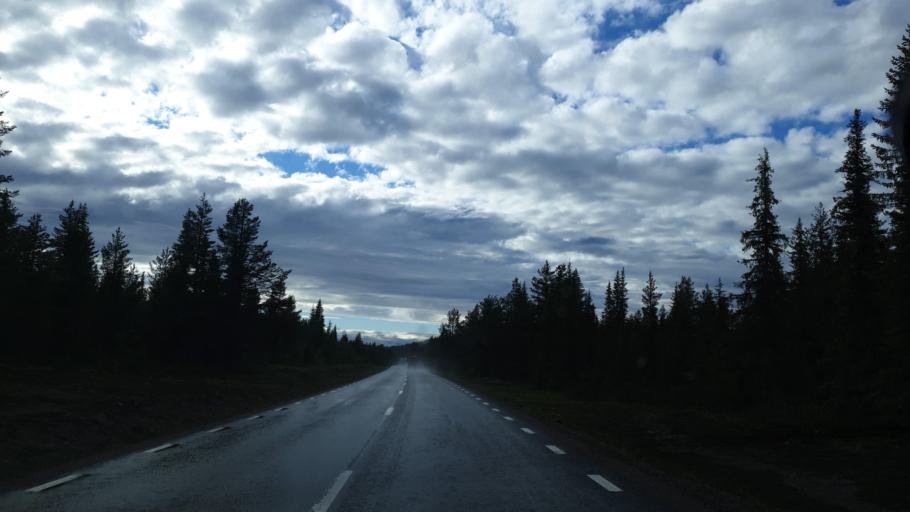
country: SE
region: Norrbotten
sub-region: Arjeplogs Kommun
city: Arjeplog
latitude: 65.9147
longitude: 18.3311
